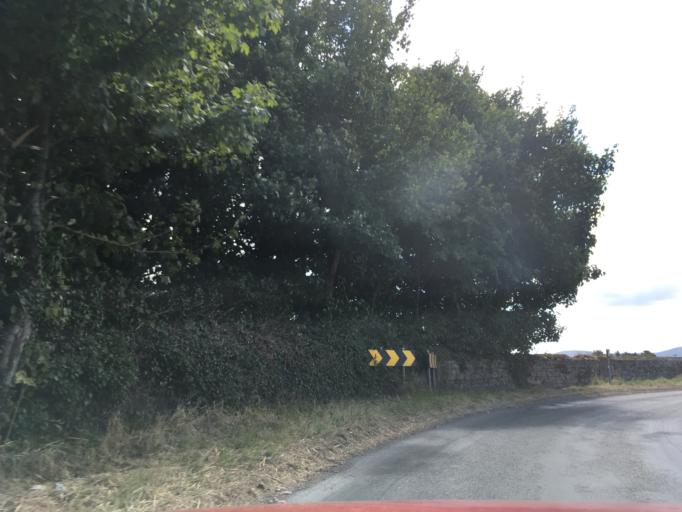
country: IE
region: Munster
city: Cahir
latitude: 52.3516
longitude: -7.9347
